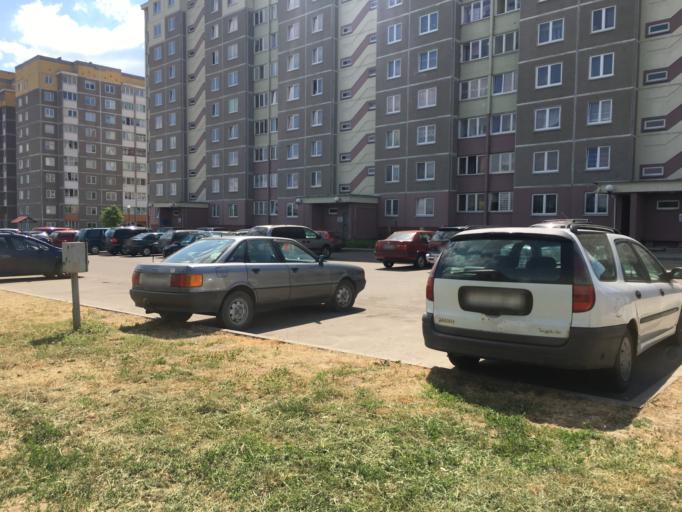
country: BY
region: Grodnenskaya
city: Hrodna
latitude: 53.7159
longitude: 23.8441
